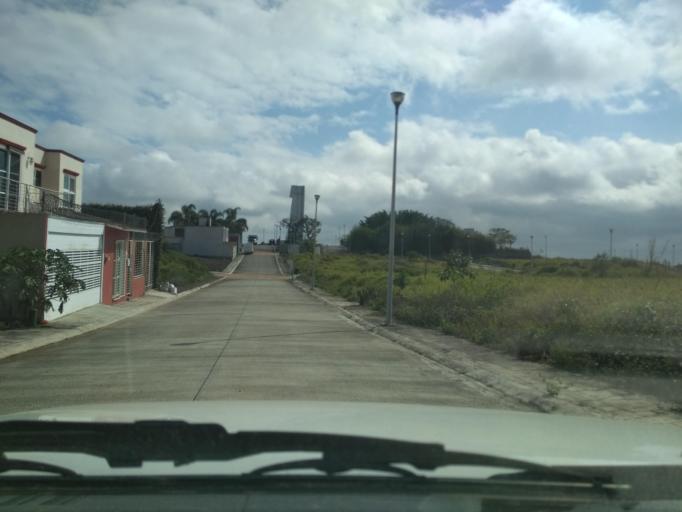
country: MX
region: Veracruz
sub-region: Emiliano Zapata
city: Jacarandas
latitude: 19.4985
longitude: -96.8409
